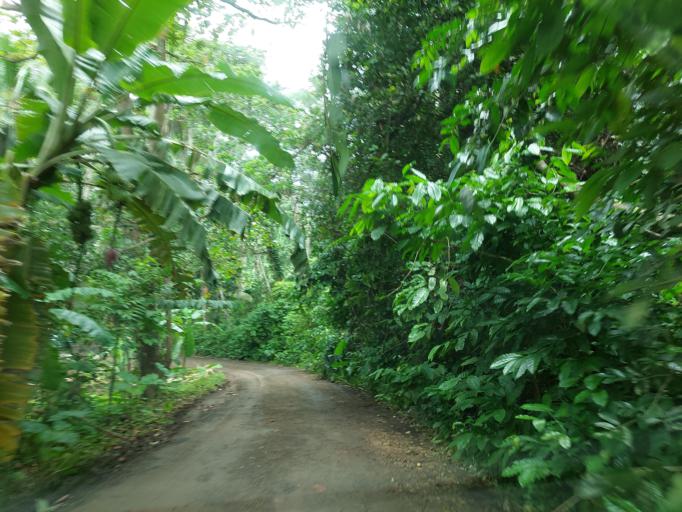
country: YT
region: Tsingoni
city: Tsingoni
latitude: -12.7617
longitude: 45.1235
